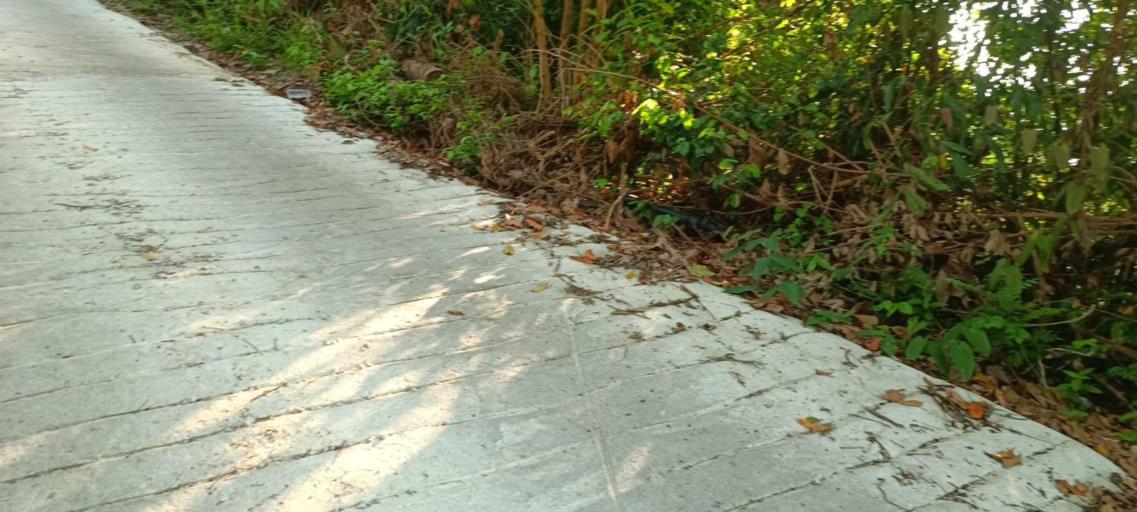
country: MY
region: Perak
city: Parit Buntar
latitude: 5.1238
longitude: 100.5521
